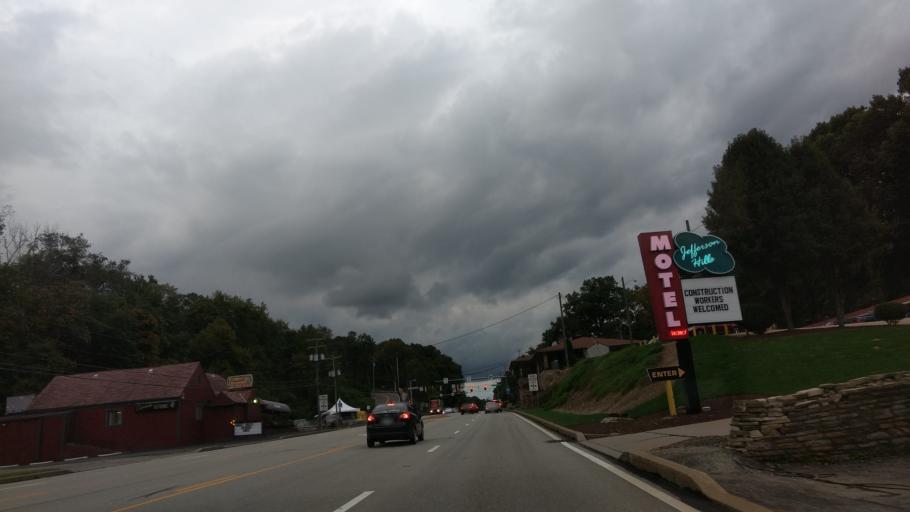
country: US
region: Pennsylvania
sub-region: Allegheny County
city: Jefferson Hills
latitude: 40.3117
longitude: -79.9380
